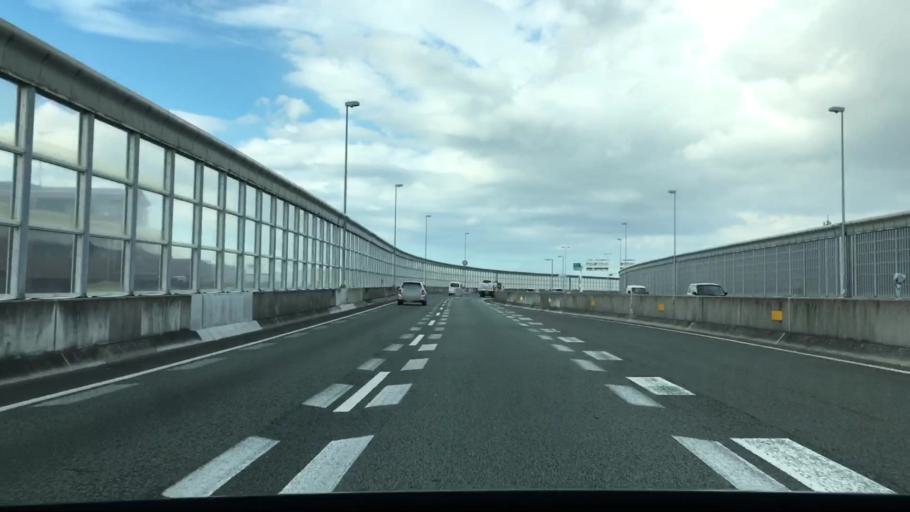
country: JP
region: Fukuoka
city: Fukuoka-shi
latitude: 33.5856
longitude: 130.3406
